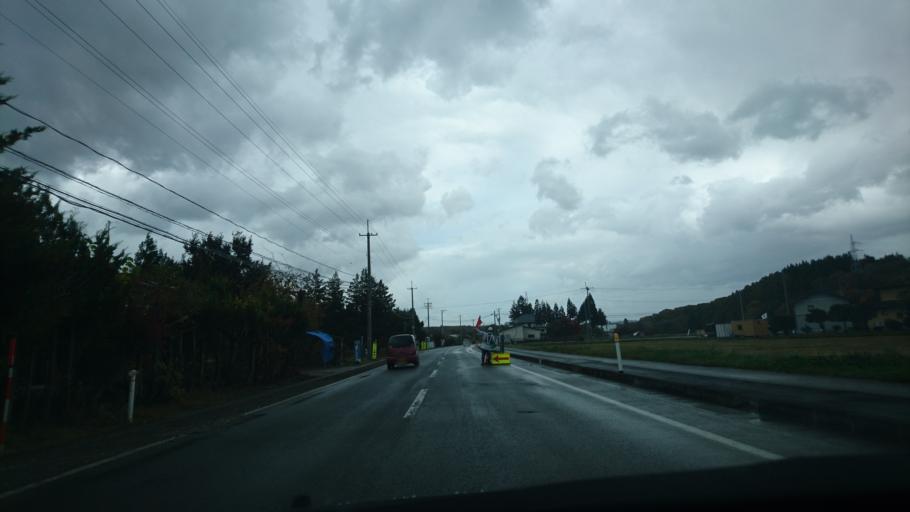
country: JP
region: Iwate
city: Shizukuishi
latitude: 39.6594
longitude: 140.9628
